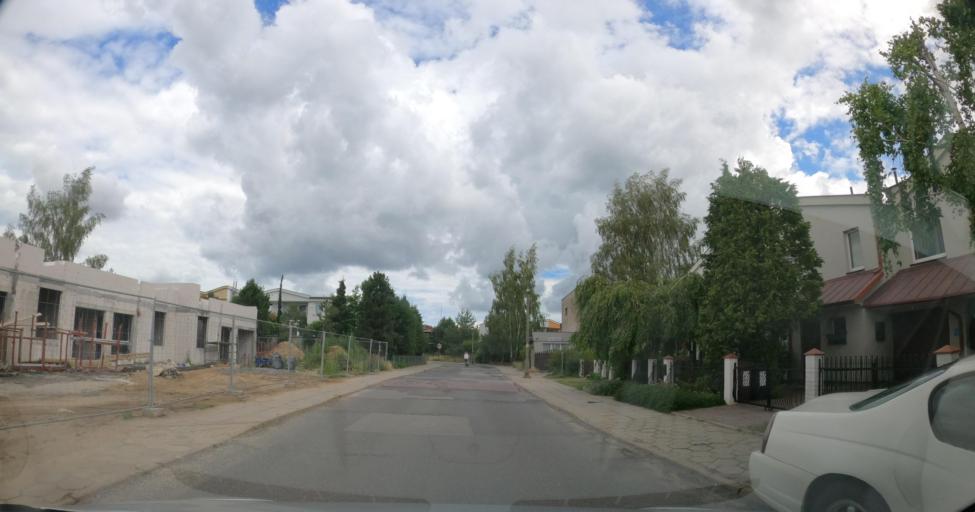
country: PL
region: Pomeranian Voivodeship
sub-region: Gdynia
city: Wielki Kack
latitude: 54.4281
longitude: 18.4735
